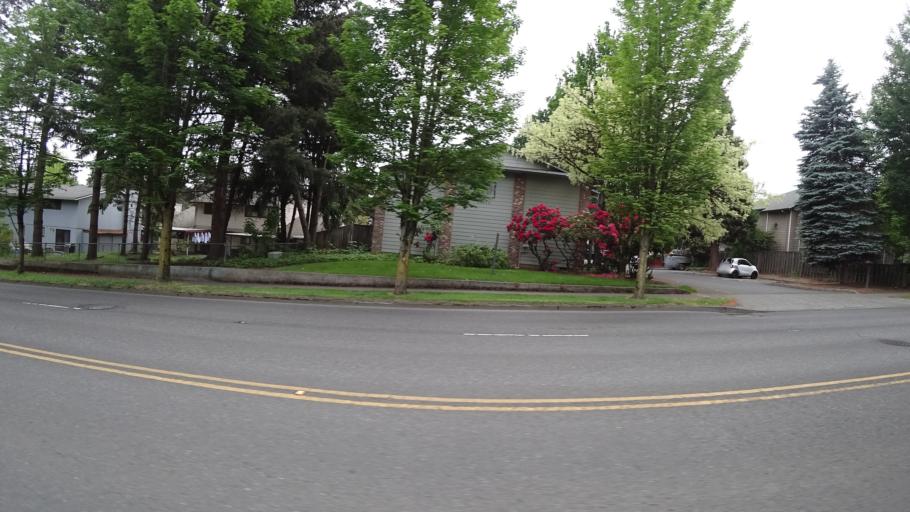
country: US
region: Oregon
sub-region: Washington County
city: Beaverton
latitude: 45.4765
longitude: -122.8207
